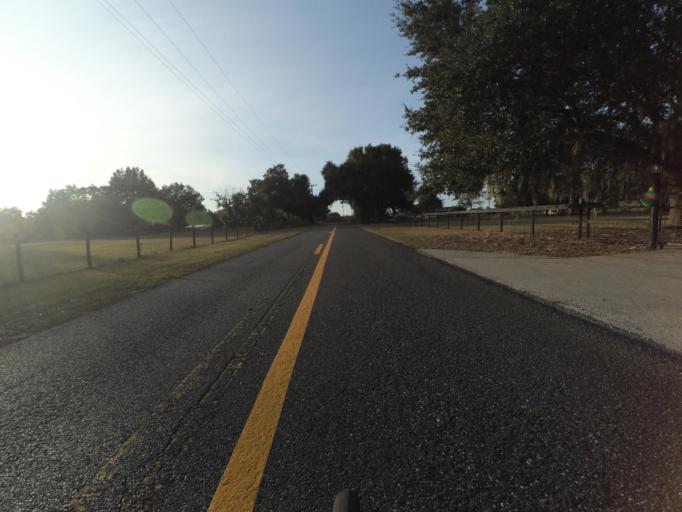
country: US
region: Florida
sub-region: Lake County
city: Umatilla
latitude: 28.9383
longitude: -81.7040
